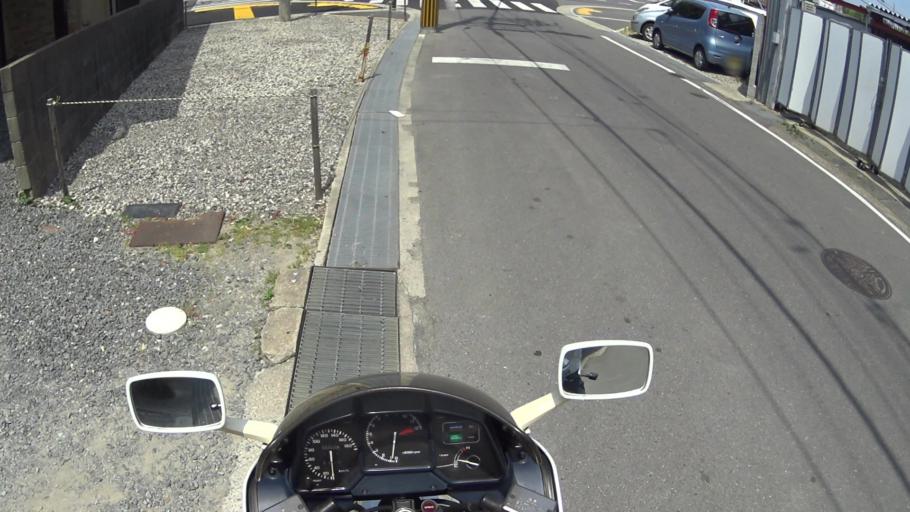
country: JP
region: Kyoto
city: Muko
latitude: 34.9429
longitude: 135.6860
